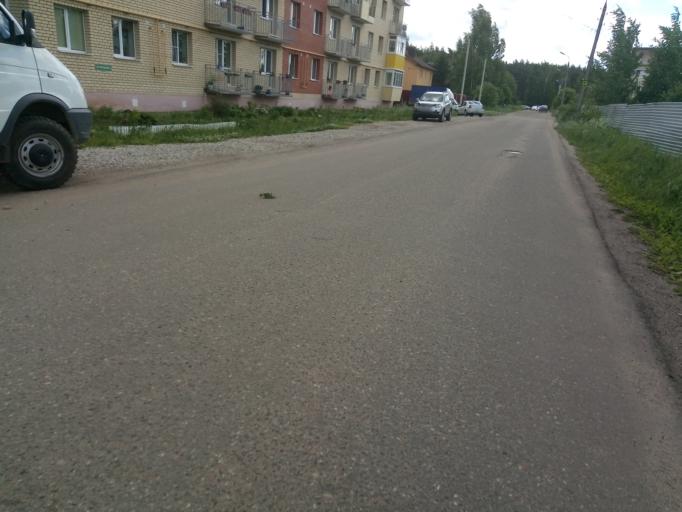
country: RU
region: Jaroslavl
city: Yaroslavl
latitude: 57.6561
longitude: 39.9802
